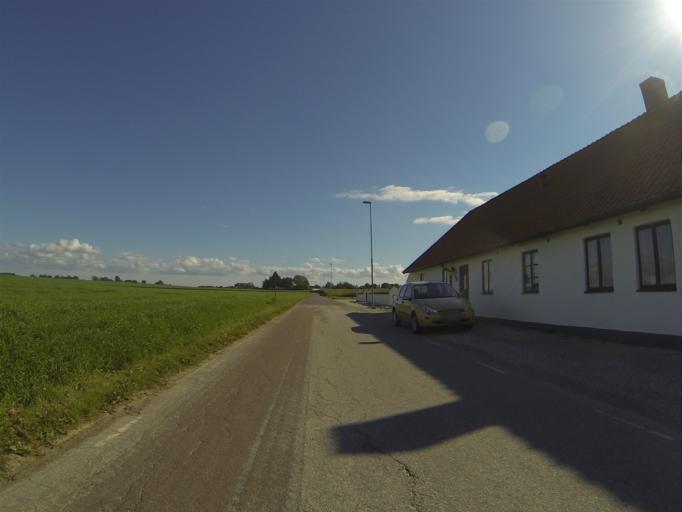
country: SE
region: Skane
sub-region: Staffanstorps Kommun
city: Staffanstorp
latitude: 55.6743
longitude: 13.2023
